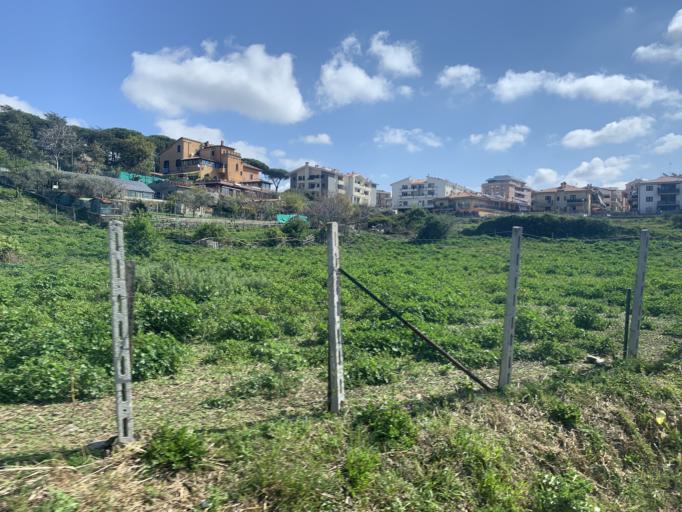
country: IT
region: Latium
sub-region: Citta metropolitana di Roma Capitale
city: Marino
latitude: 41.7703
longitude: 12.6488
